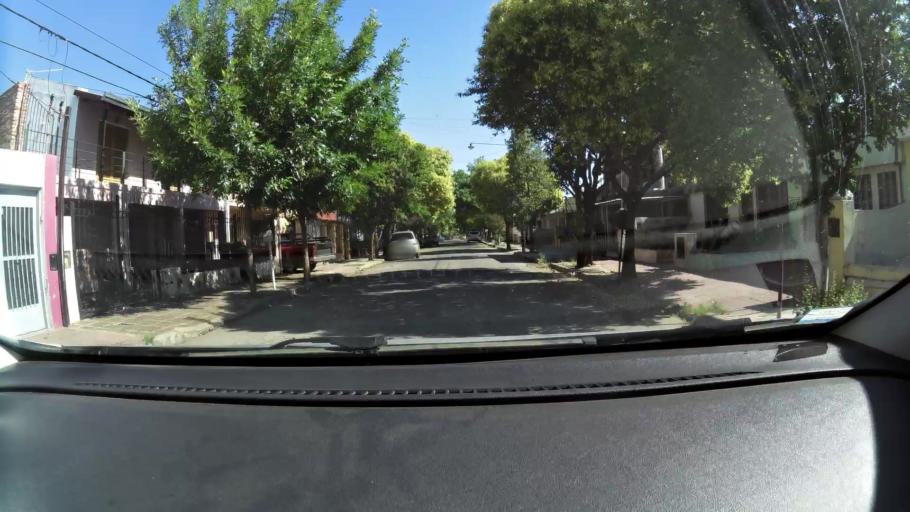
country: AR
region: Cordoba
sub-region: Departamento de Capital
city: Cordoba
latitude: -31.3728
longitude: -64.1818
